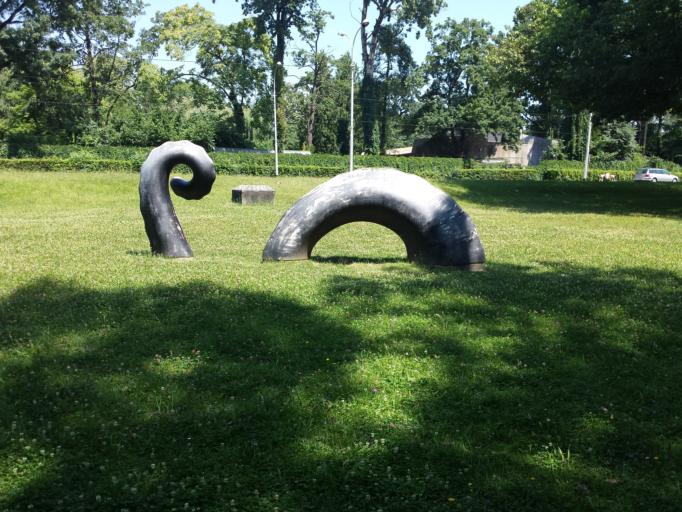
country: HR
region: Grad Zagreb
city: Zagreb
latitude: 45.8203
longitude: 16.0212
